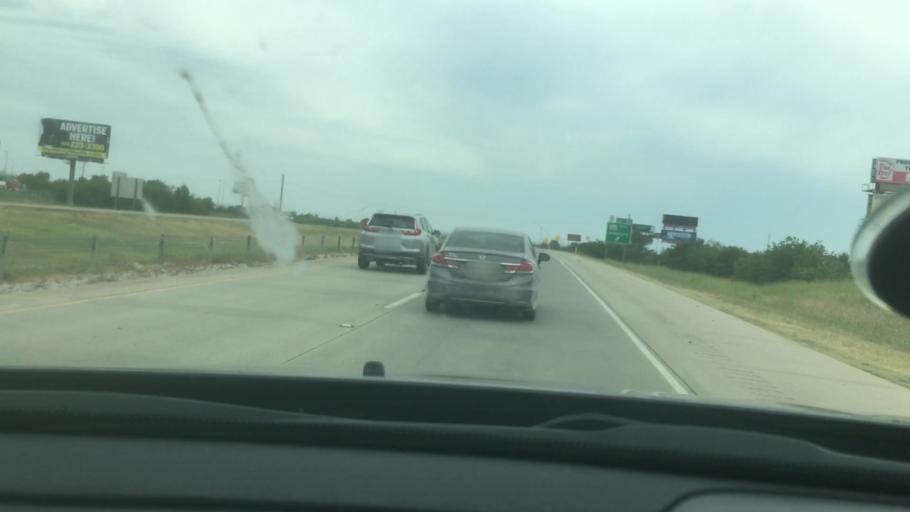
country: US
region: Oklahoma
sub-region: Carter County
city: Ardmore
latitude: 34.1956
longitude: -97.1639
